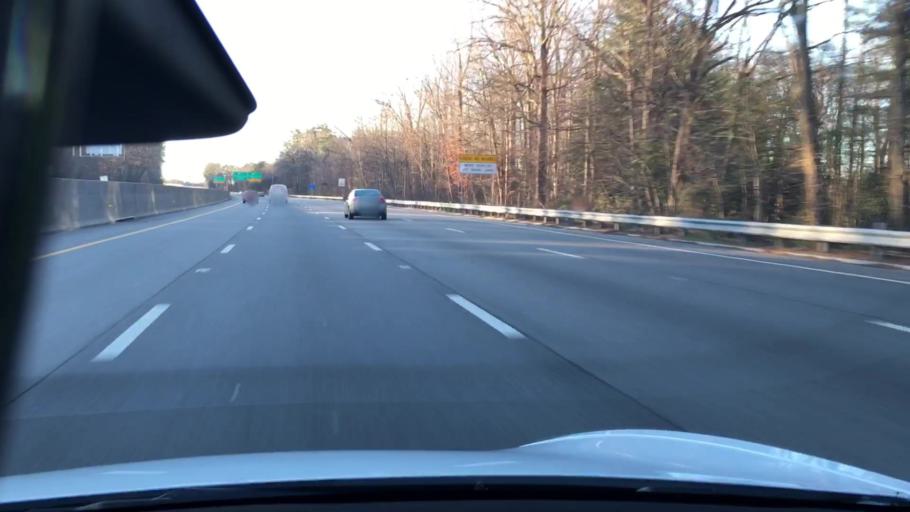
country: US
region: Virginia
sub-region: Chesterfield County
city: Bon Air
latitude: 37.5115
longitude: -77.5274
